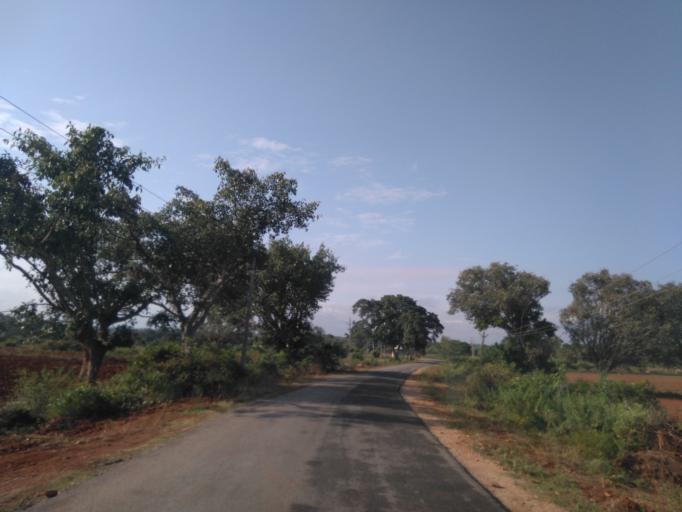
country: IN
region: Karnataka
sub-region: Mandya
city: Malavalli
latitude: 12.3074
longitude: 77.0726
